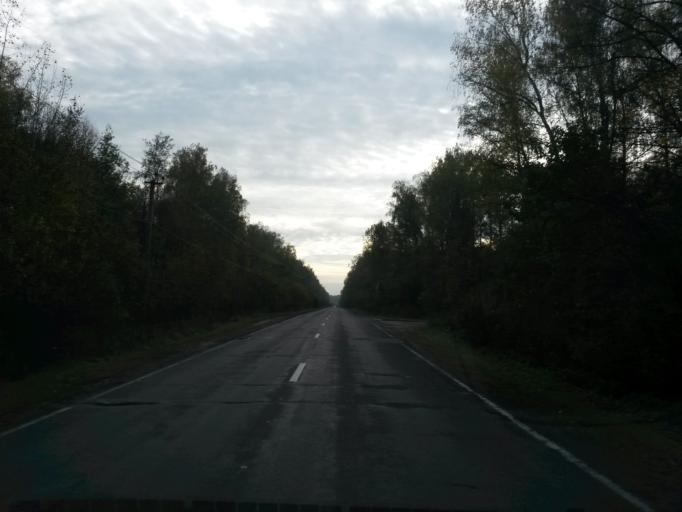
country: RU
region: Moskovskaya
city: Melikhovo
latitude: 55.2231
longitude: 37.6637
